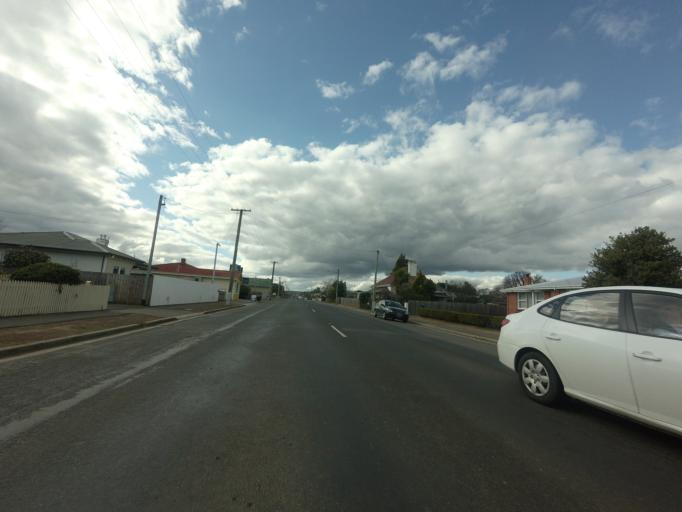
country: AU
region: Tasmania
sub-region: Northern Midlands
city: Longford
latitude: -41.6029
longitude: 147.1193
